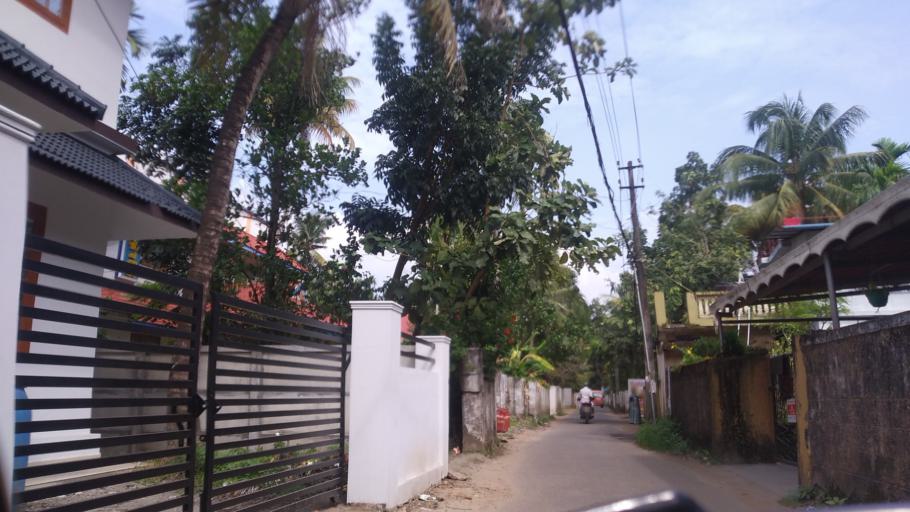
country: IN
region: Kerala
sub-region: Ernakulam
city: Elur
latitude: 10.0861
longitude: 76.2067
